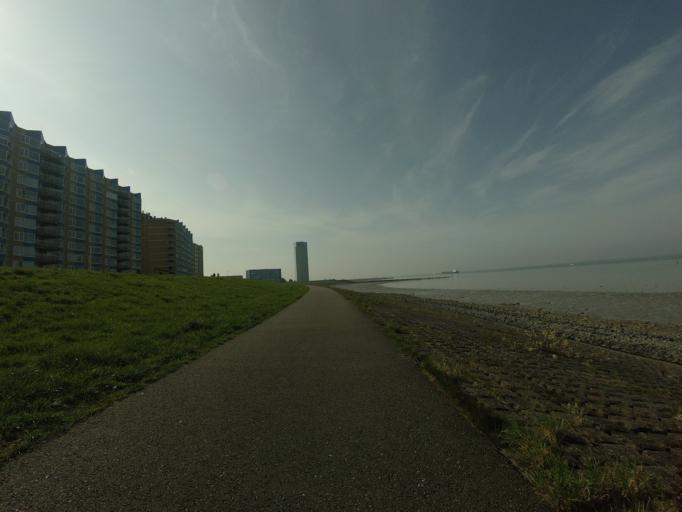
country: NL
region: Zeeland
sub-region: Gemeente Terneuzen
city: Terneuzen
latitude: 51.3361
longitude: 3.8410
